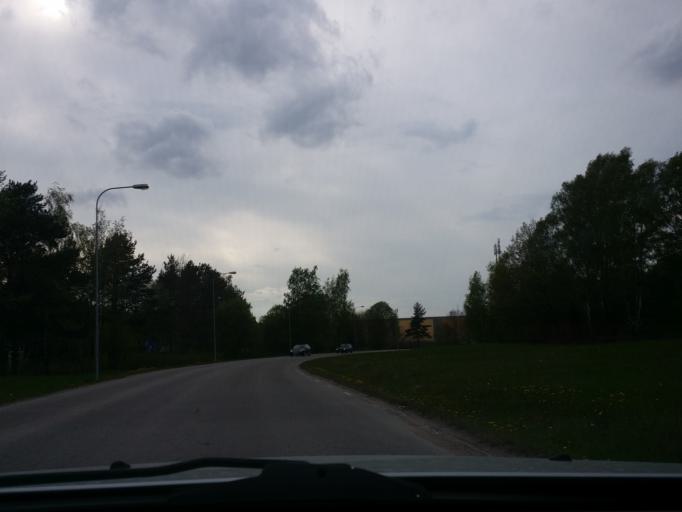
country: SE
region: Vaestmanland
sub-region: Vasteras
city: Vasteras
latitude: 59.6072
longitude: 16.6138
